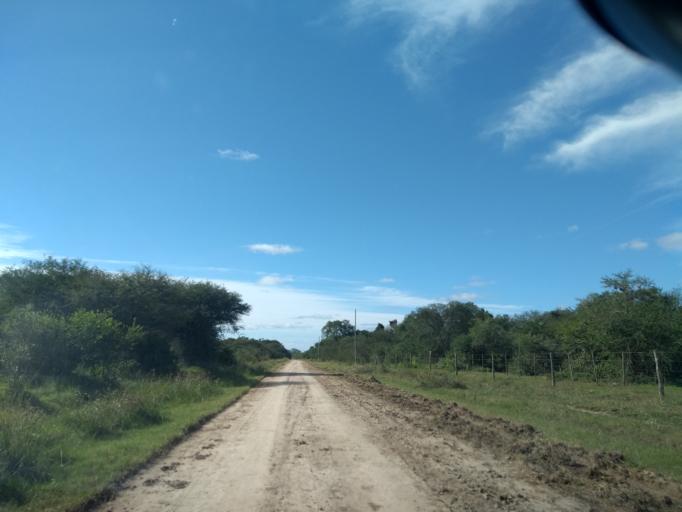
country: AR
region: Chaco
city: Colonia Benitez
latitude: -27.2852
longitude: -58.9292
